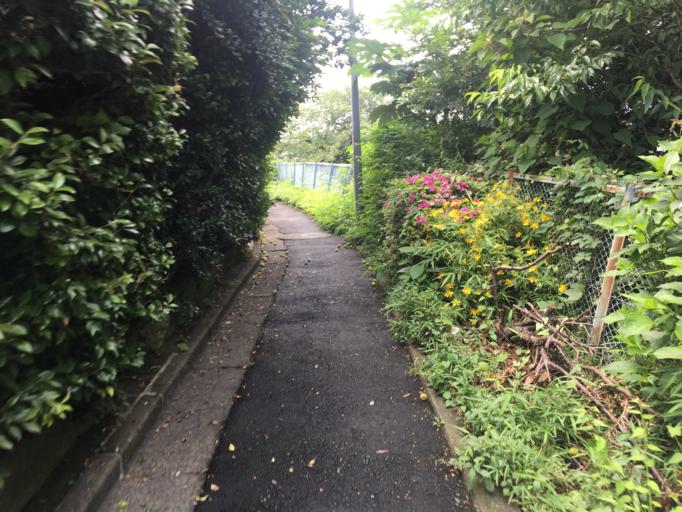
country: JP
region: Saitama
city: Kawaguchi
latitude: 35.7759
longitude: 139.7183
